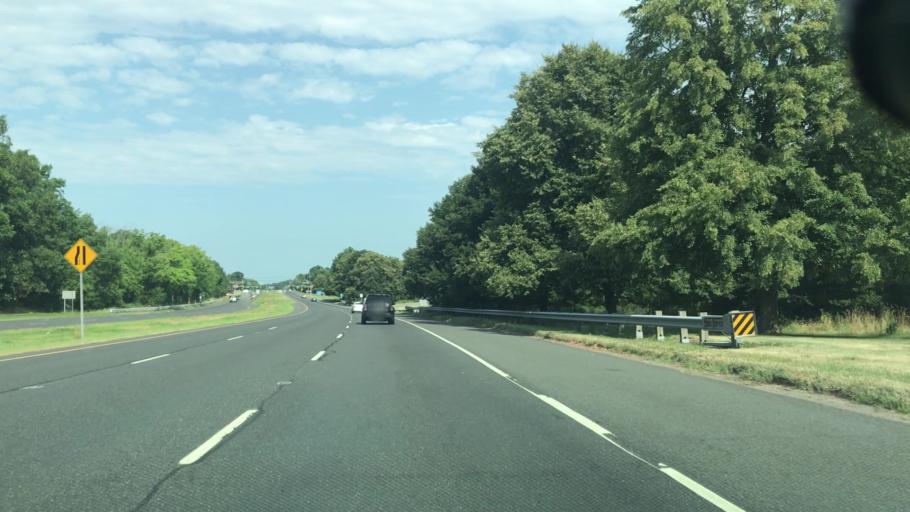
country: US
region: New Jersey
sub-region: Somerset County
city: Raritan
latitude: 40.5864
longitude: -74.6343
